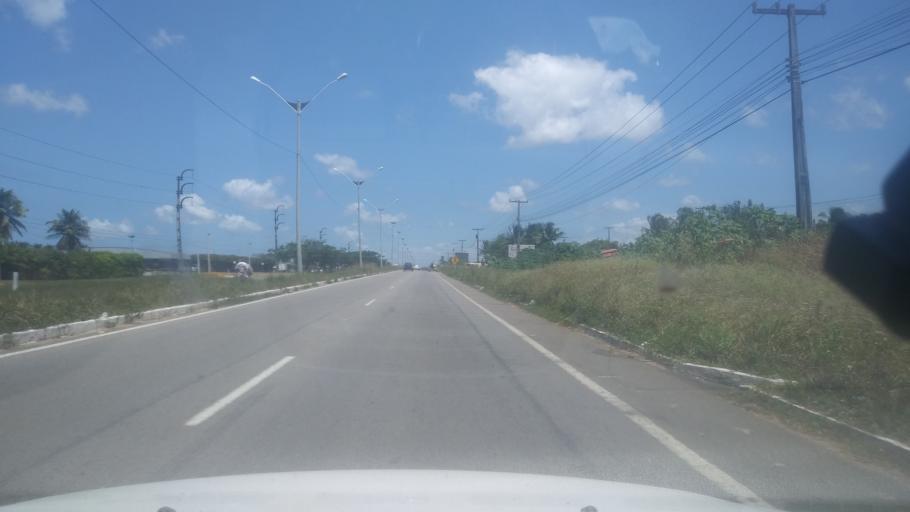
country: BR
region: Rio Grande do Norte
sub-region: Extremoz
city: Extremoz
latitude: -5.7477
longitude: -35.2896
